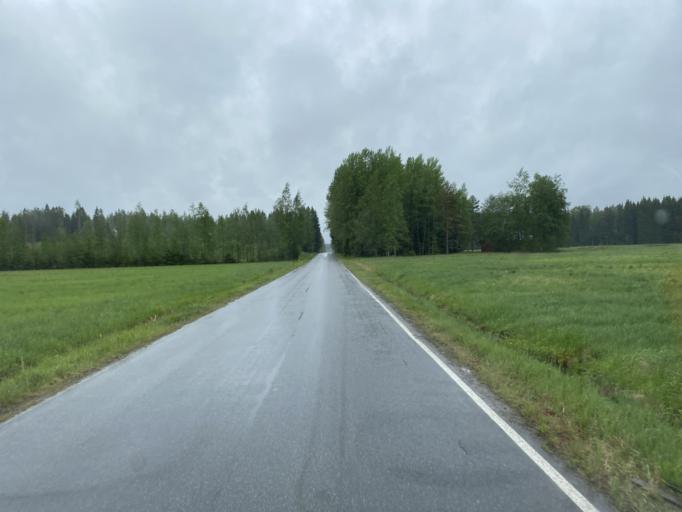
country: FI
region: Haeme
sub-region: Forssa
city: Humppila
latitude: 61.0629
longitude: 23.3242
